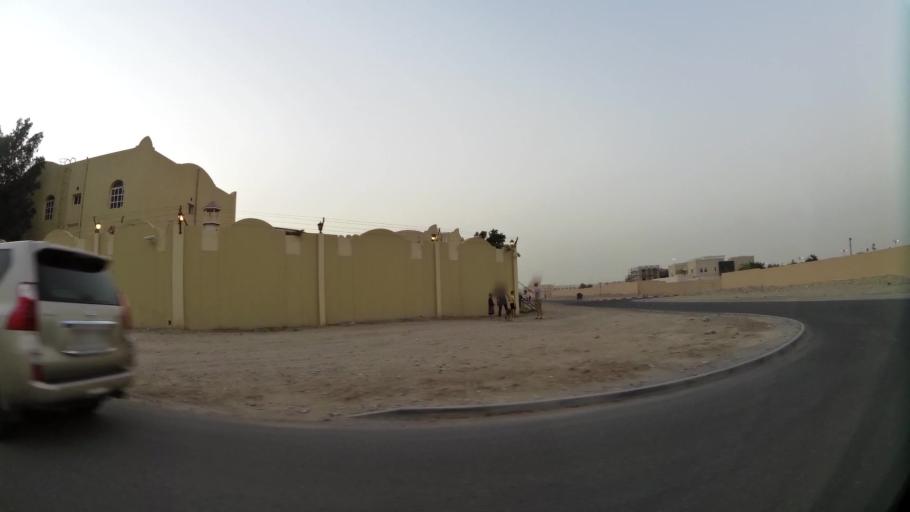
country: QA
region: Baladiyat ar Rayyan
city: Ar Rayyan
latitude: 25.2554
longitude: 51.4666
